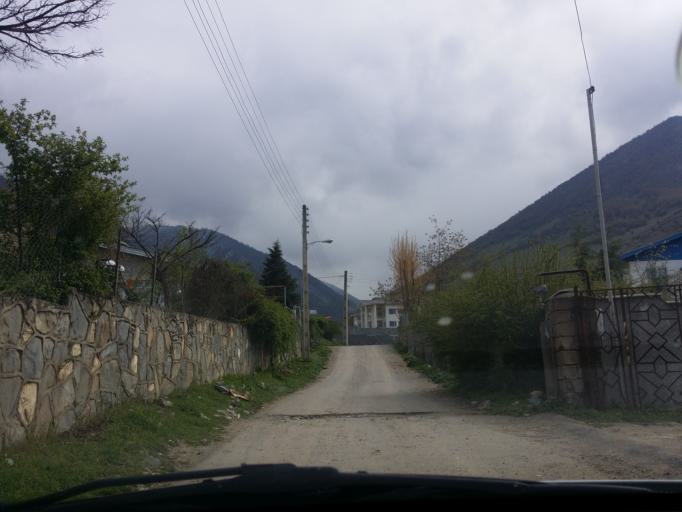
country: IR
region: Mazandaran
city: `Abbasabad
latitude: 36.4816
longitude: 51.1395
